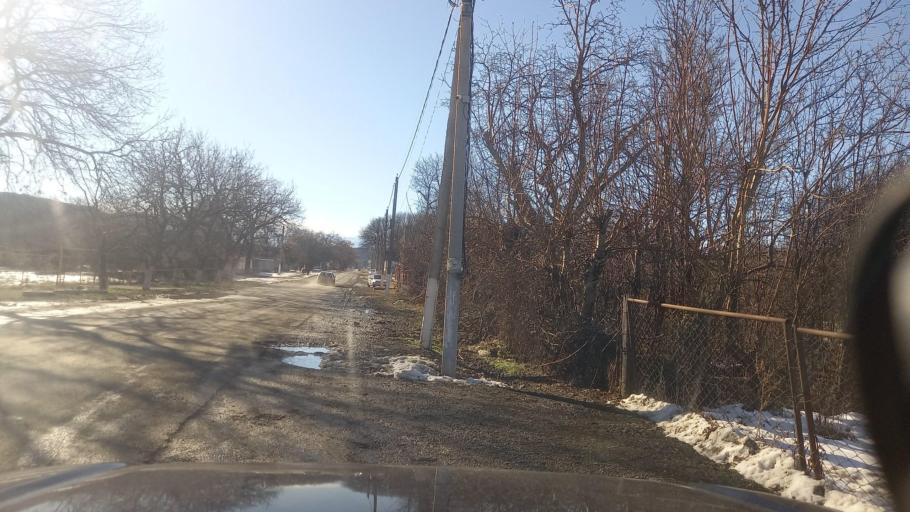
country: RU
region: Kabardino-Balkariya
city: Urukh
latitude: 43.2730
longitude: 43.9975
